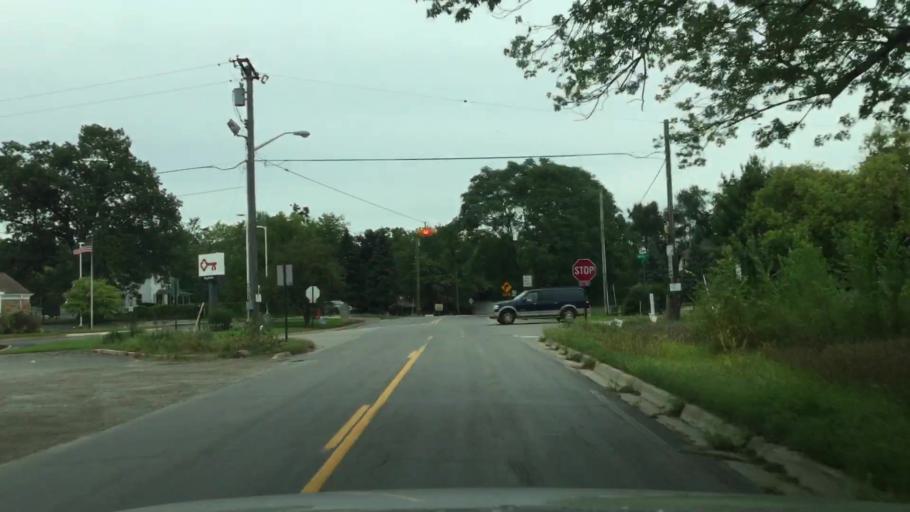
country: US
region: Michigan
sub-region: Washtenaw County
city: Milan
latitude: 42.1557
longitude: -83.6531
